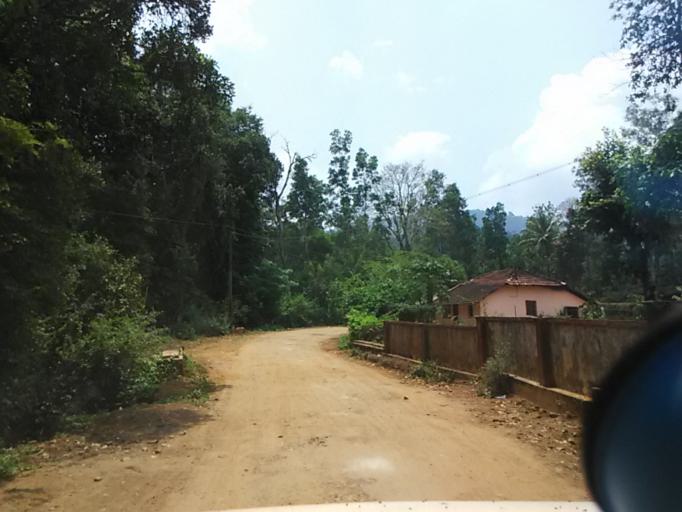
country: IN
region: Karnataka
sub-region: Kodagu
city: Virarajendrapet
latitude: 12.2099
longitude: 75.6762
